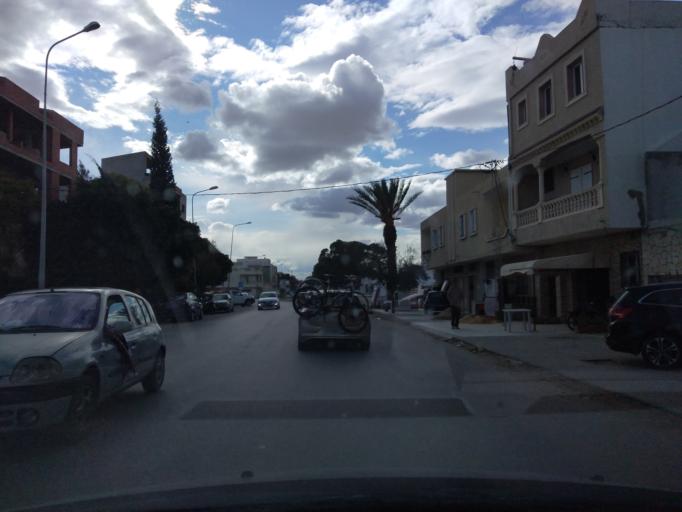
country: TN
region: Susah
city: Masakin
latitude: 35.7197
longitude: 10.5656
